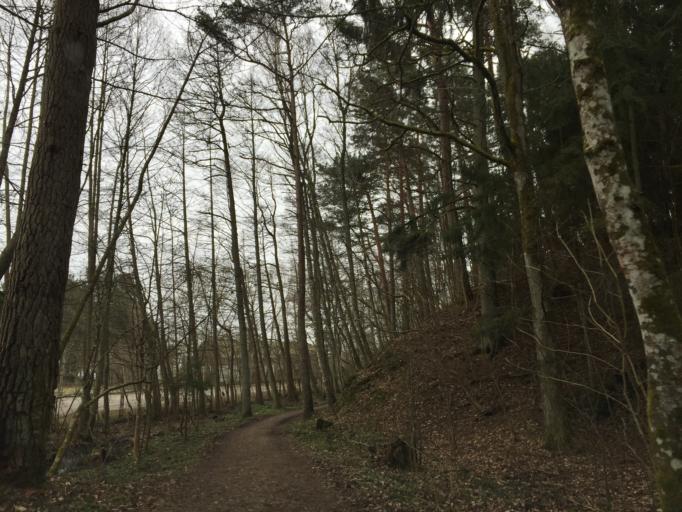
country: LT
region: Klaipedos apskritis
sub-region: Klaipeda
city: Klaipeda
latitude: 55.5552
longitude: 21.1244
